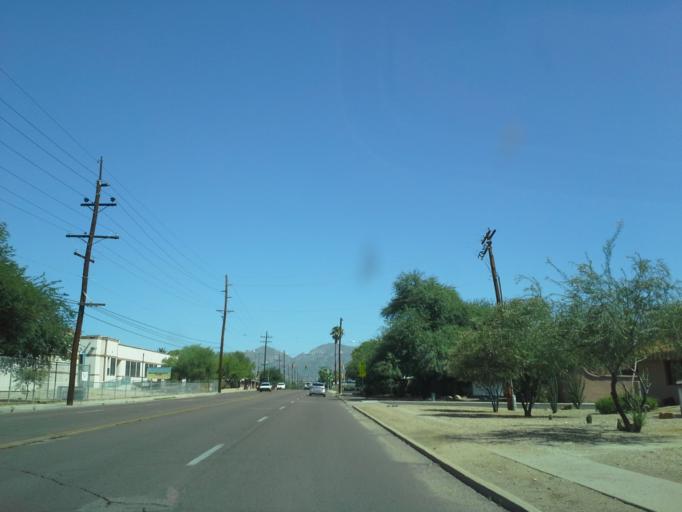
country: US
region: Arizona
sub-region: Pima County
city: Tucson
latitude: 32.2415
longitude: -110.9267
